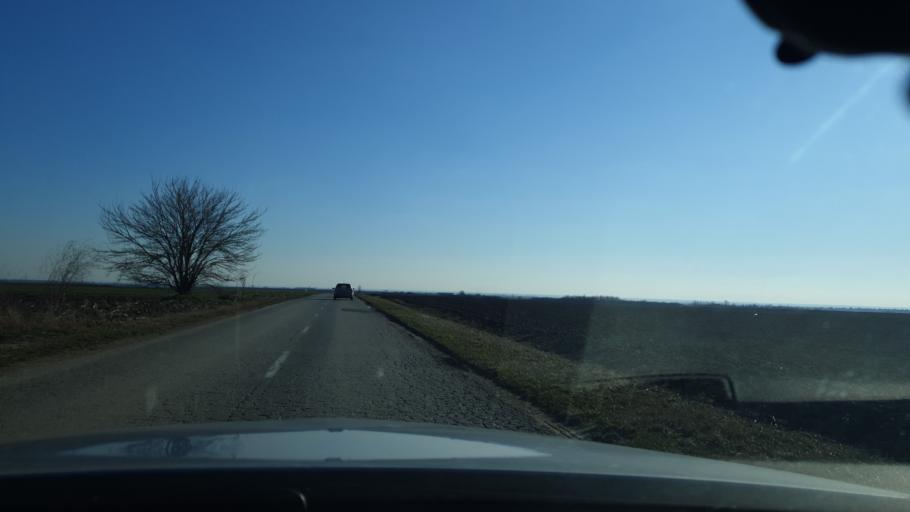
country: RS
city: Vrdnik
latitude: 45.0775
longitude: 19.8083
